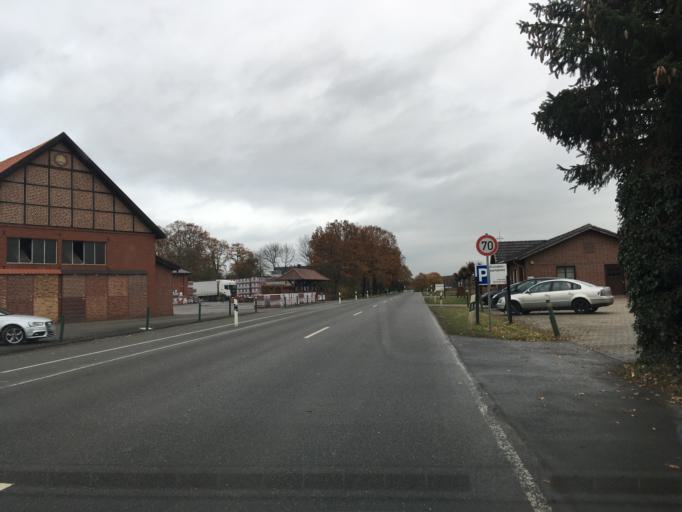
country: DE
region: North Rhine-Westphalia
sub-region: Regierungsbezirk Munster
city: Gescher
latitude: 51.9703
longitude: 7.0138
